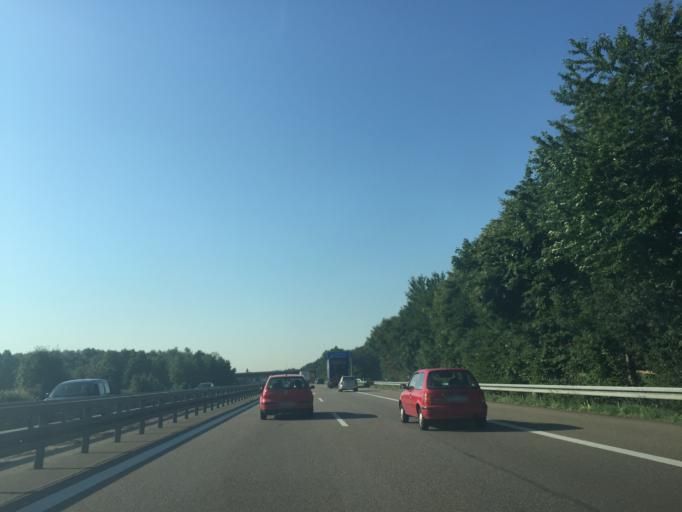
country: DE
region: Baden-Wuerttemberg
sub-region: Karlsruhe Region
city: Schriesheim
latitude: 49.4811
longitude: 8.6392
